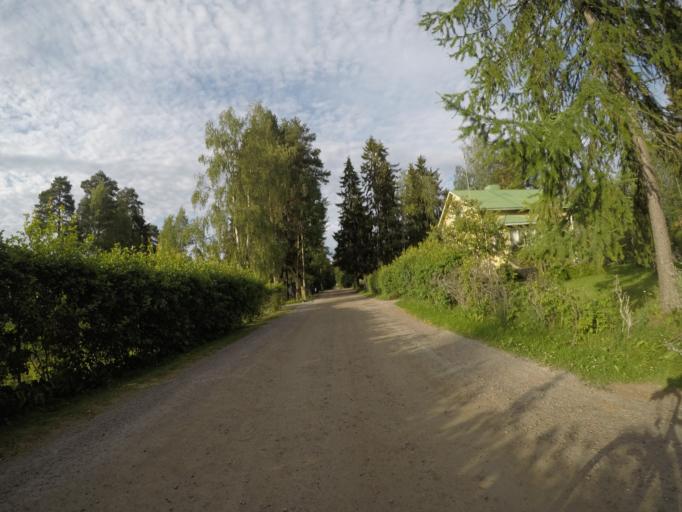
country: FI
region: Haeme
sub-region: Haemeenlinna
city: Haemeenlinna
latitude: 60.9788
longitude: 24.4085
